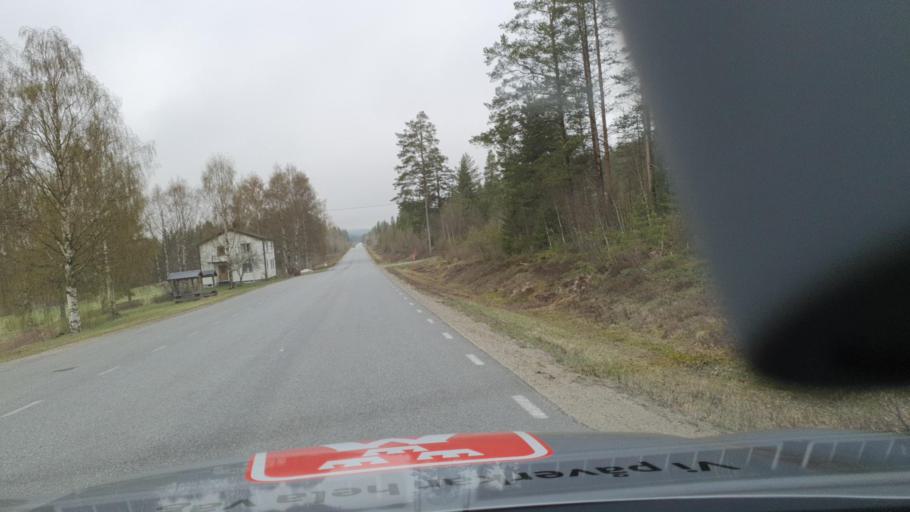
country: SE
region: Vaesternorrland
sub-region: OErnskoeldsviks Kommun
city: Husum
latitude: 63.5413
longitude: 19.0887
